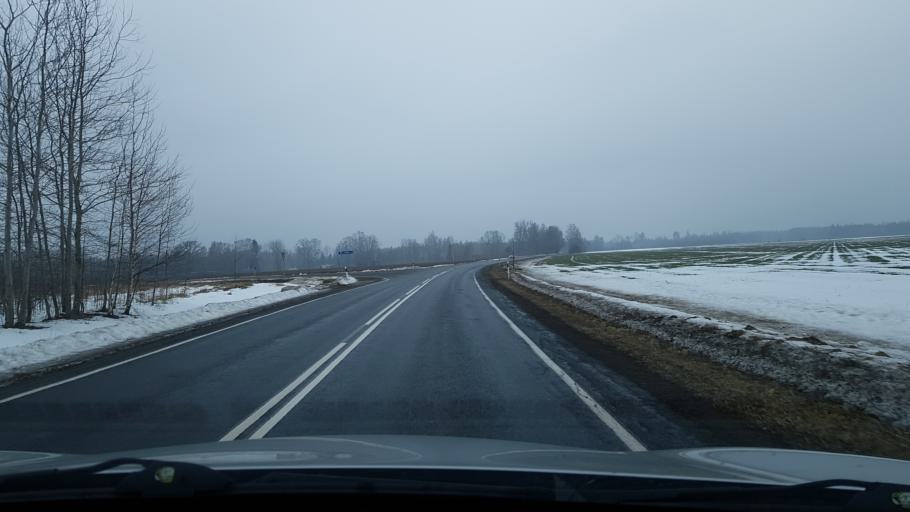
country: EE
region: Valgamaa
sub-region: Torva linn
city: Torva
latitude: 58.1538
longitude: 25.9657
